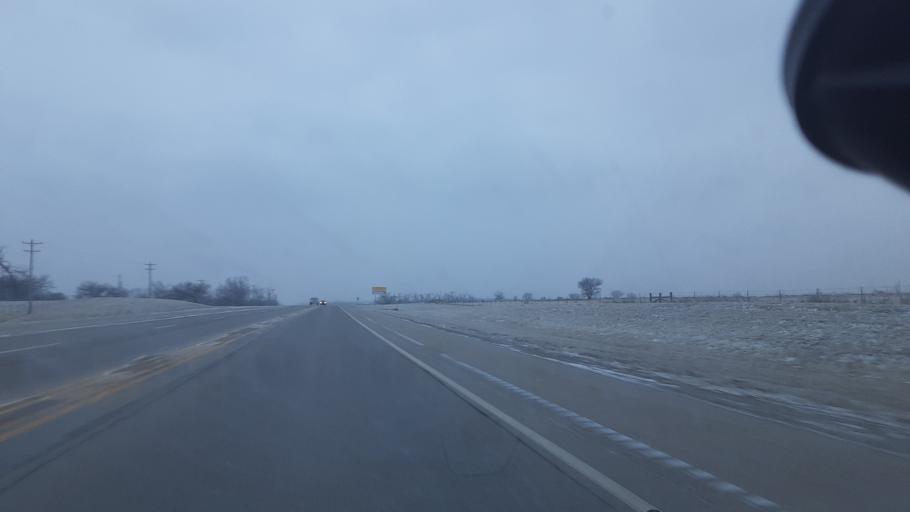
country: US
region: Oklahoma
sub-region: Payne County
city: Perkins
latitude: 35.9854
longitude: -97.0937
